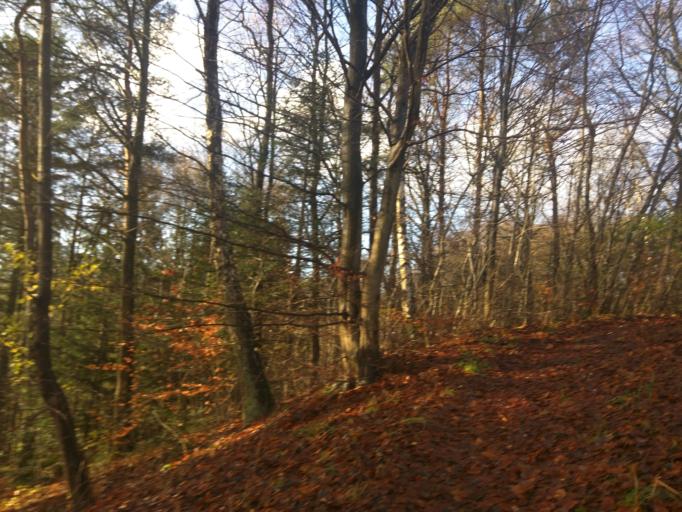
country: DK
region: Central Jutland
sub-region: Silkeborg Kommune
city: Silkeborg
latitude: 56.1882
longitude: 9.5294
